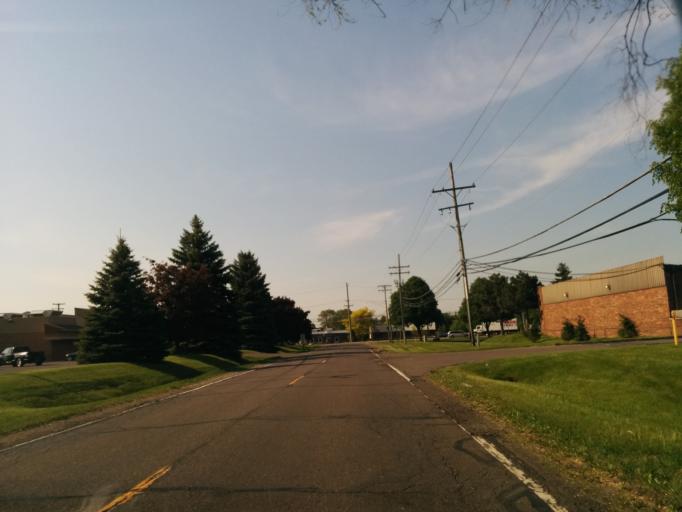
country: US
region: Michigan
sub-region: Oakland County
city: Novi
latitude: 42.4754
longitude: -83.4454
